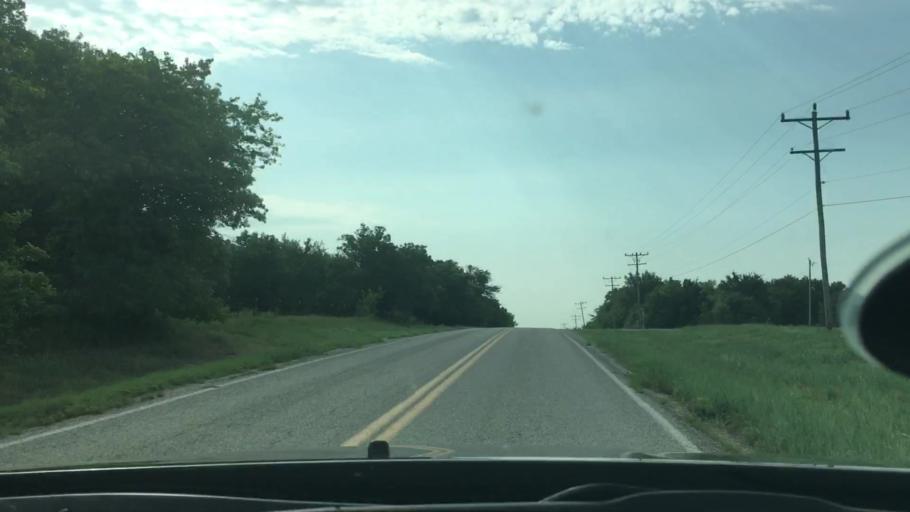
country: US
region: Oklahoma
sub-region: Johnston County
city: Tishomingo
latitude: 34.1492
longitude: -96.5541
